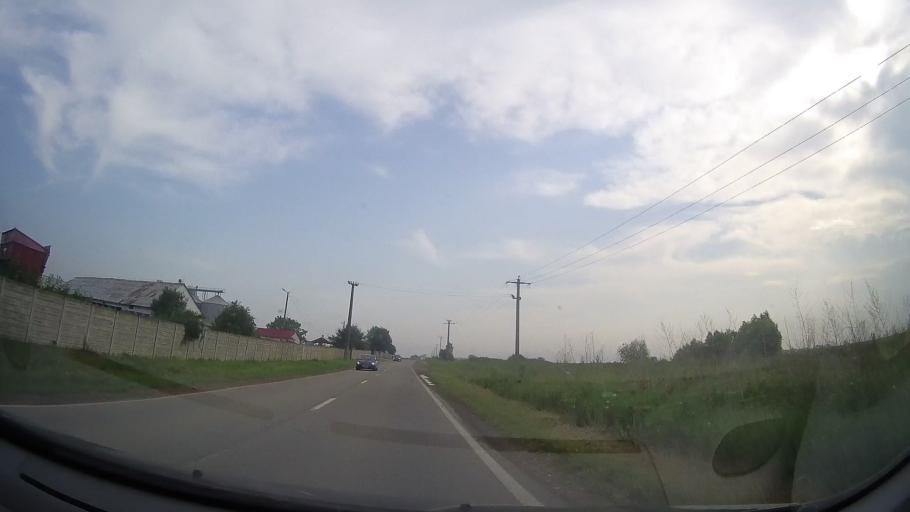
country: RO
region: Timis
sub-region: Comuna Sag
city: Sag
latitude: 45.6616
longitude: 21.1502
